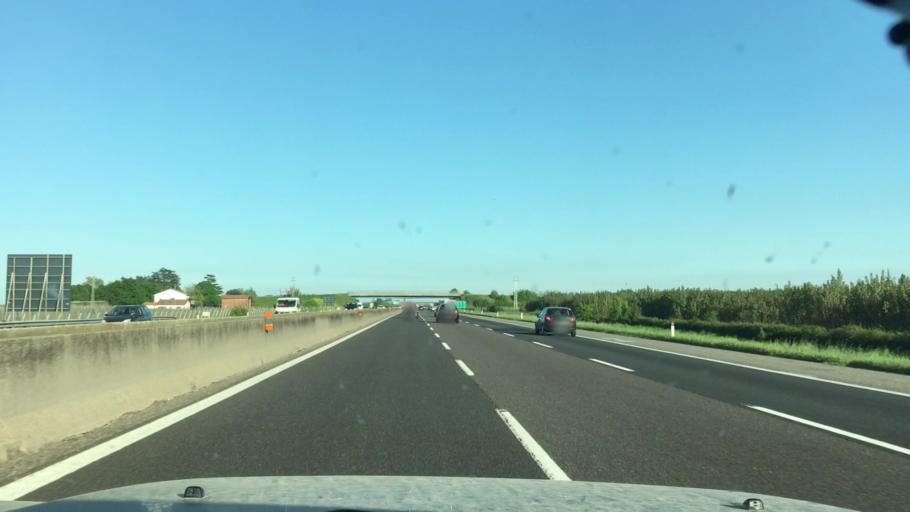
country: IT
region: Emilia-Romagna
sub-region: Provincia di Bologna
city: Imola
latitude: 44.3778
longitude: 11.7501
